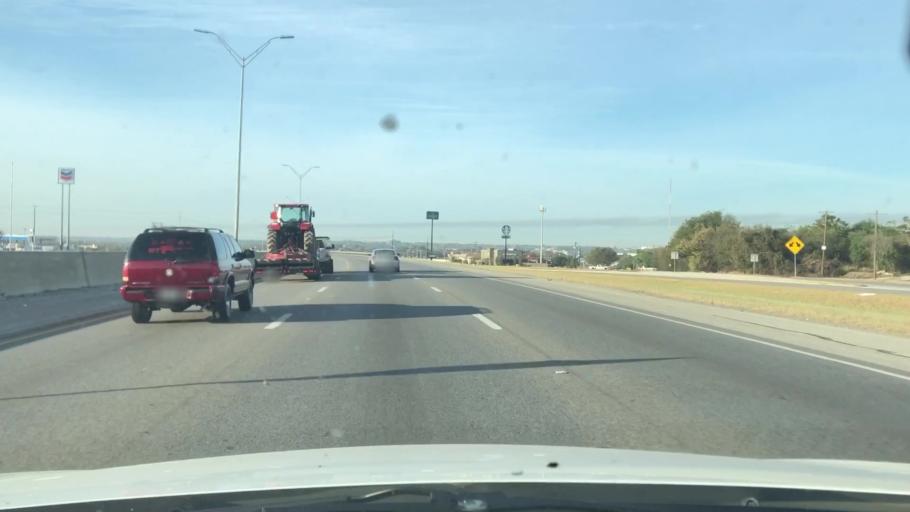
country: US
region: Texas
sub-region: Bexar County
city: Kirby
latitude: 29.4274
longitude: -98.4194
